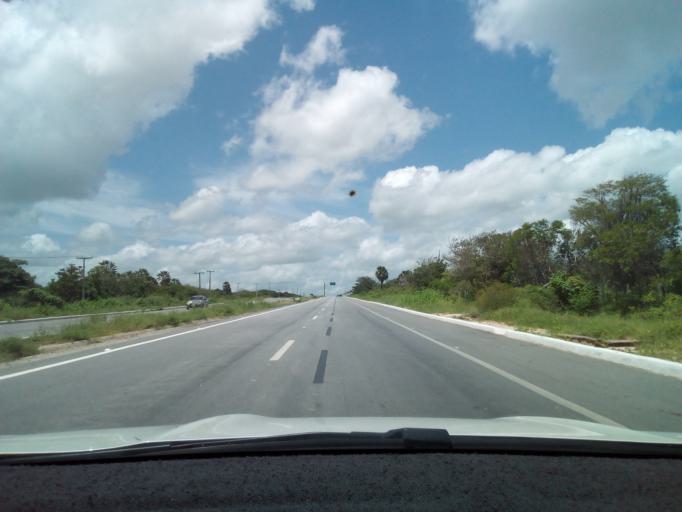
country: BR
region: Ceara
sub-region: Aracati
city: Aracati
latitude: -4.5534
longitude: -37.7972
